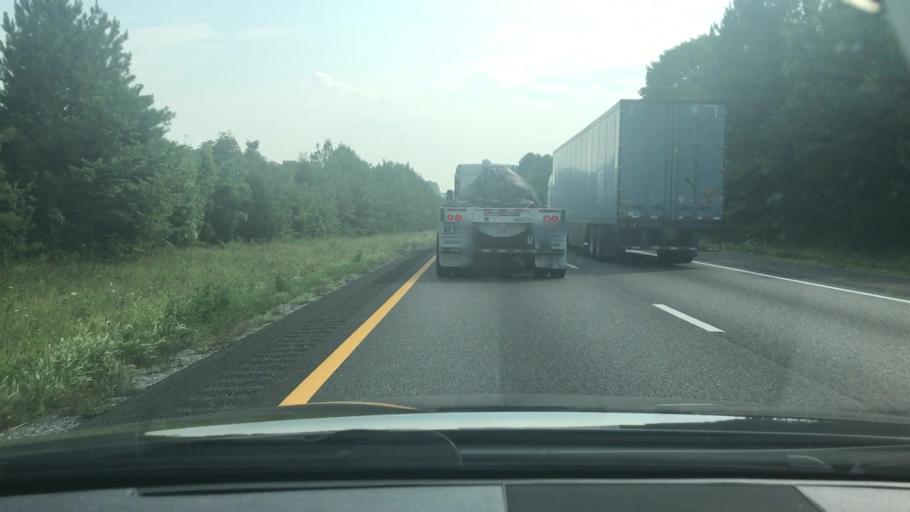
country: US
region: Tennessee
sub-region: Sumner County
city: White House
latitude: 36.4471
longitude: -86.6991
